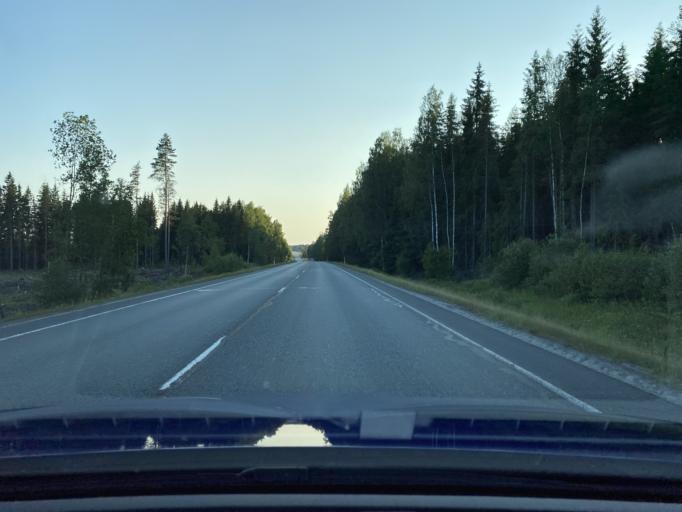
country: FI
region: Haeme
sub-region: Forssa
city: Tammela
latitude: 60.8299
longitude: 23.8562
